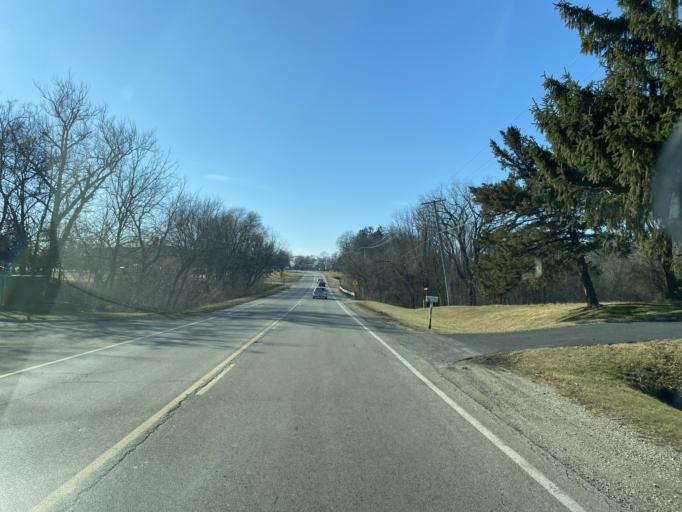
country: US
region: Illinois
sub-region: Will County
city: Lockport
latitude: 41.6071
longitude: -88.0471
